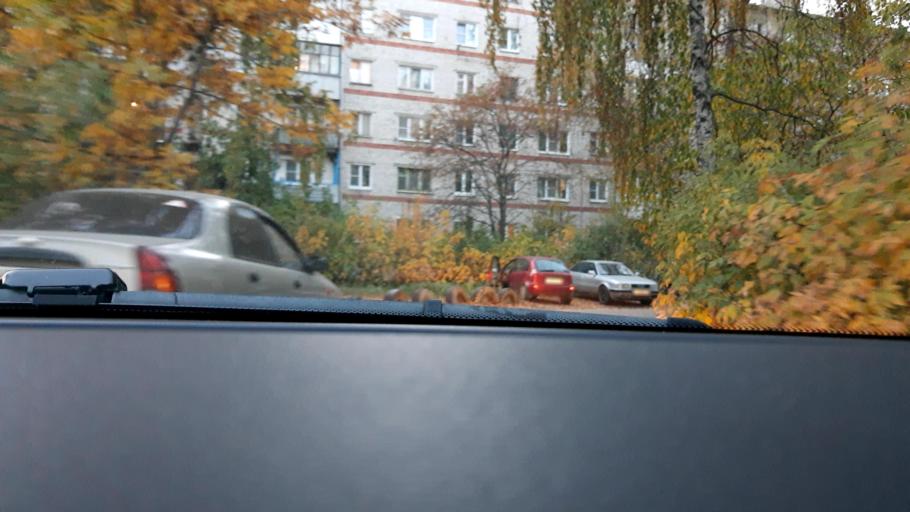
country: RU
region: Nizjnij Novgorod
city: Gorbatovka
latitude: 56.3283
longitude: 43.8413
